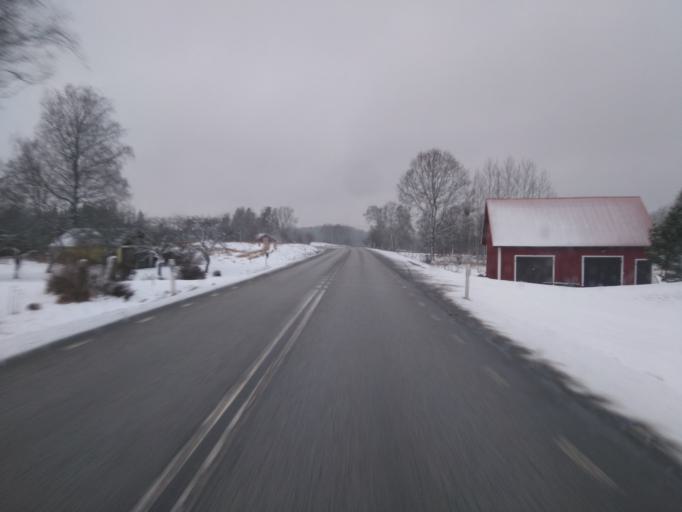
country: SE
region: Joenkoeping
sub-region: Eksjo Kommun
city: Eksjoe
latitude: 57.6401
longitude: 15.0838
